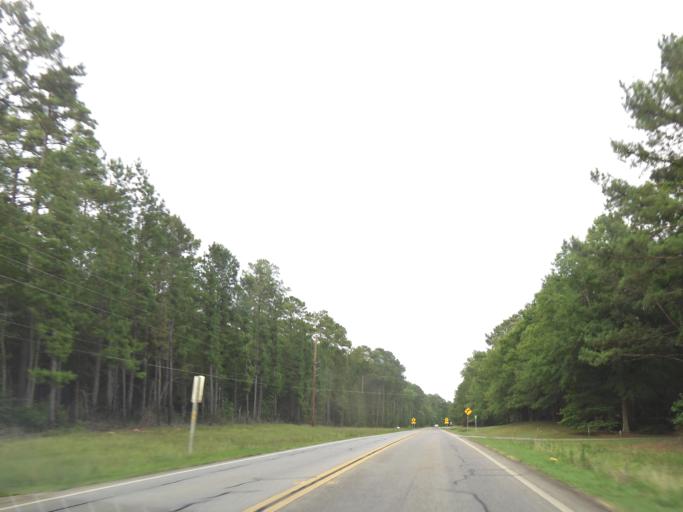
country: US
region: Georgia
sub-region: Bibb County
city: West Point
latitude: 32.8645
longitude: -83.8140
